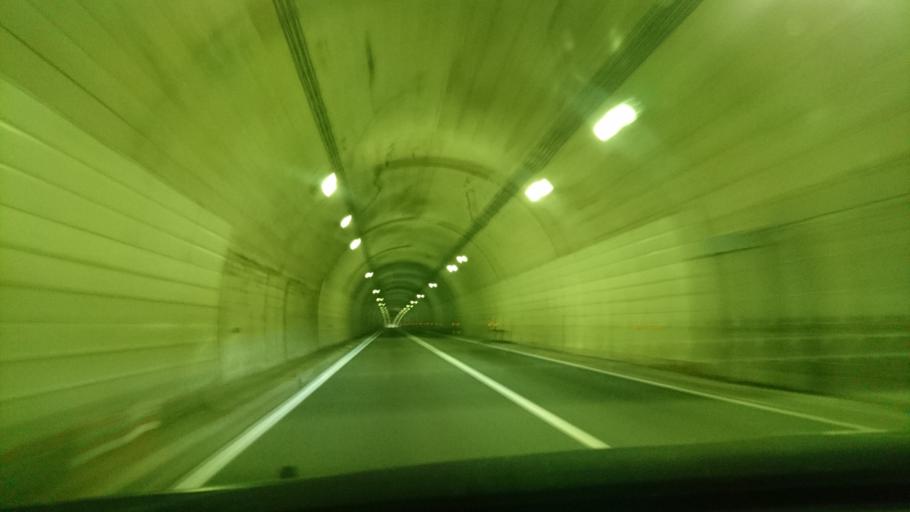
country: JP
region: Akita
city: Yokotemachi
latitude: 39.3118
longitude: 140.7668
